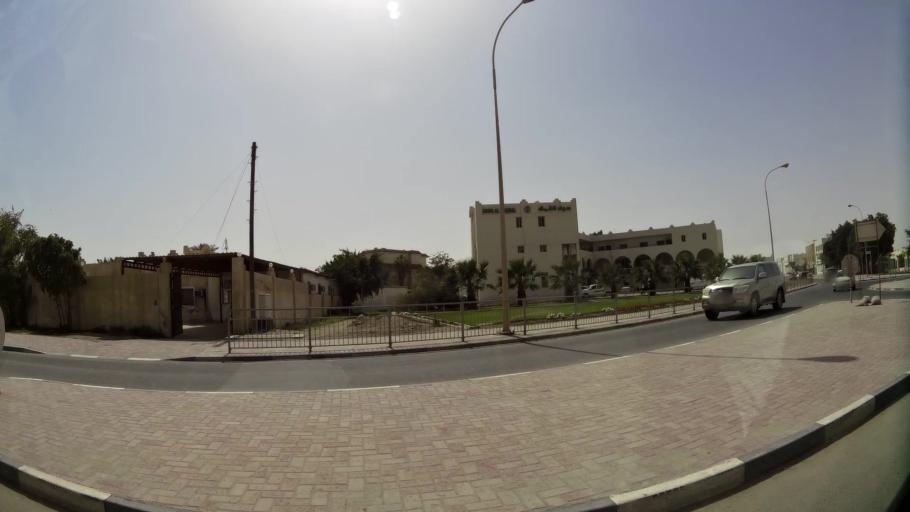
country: QA
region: Baladiyat Umm Salal
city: Umm Salal Muhammad
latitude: 25.3944
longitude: 51.4273
